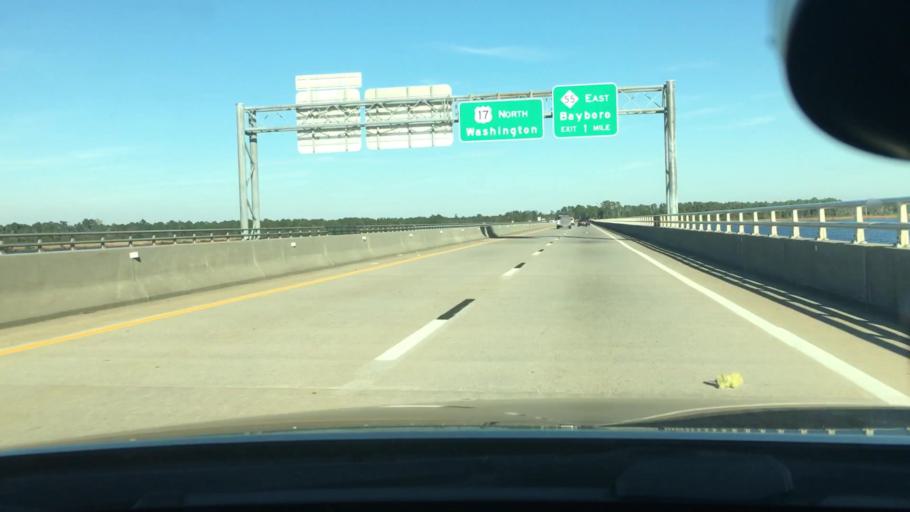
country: US
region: North Carolina
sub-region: Craven County
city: James City
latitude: 35.0987
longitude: -77.0199
